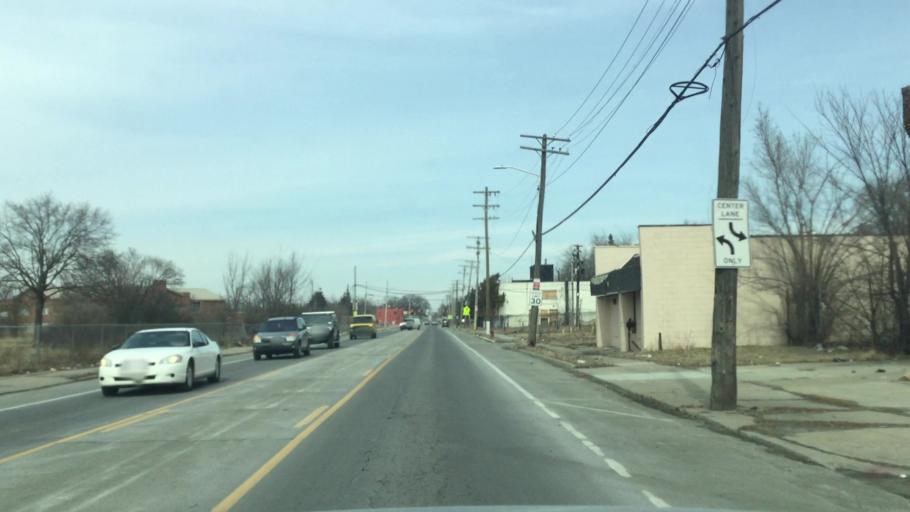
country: US
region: Michigan
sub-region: Wayne County
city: Dearborn
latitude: 42.3625
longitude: -83.1580
